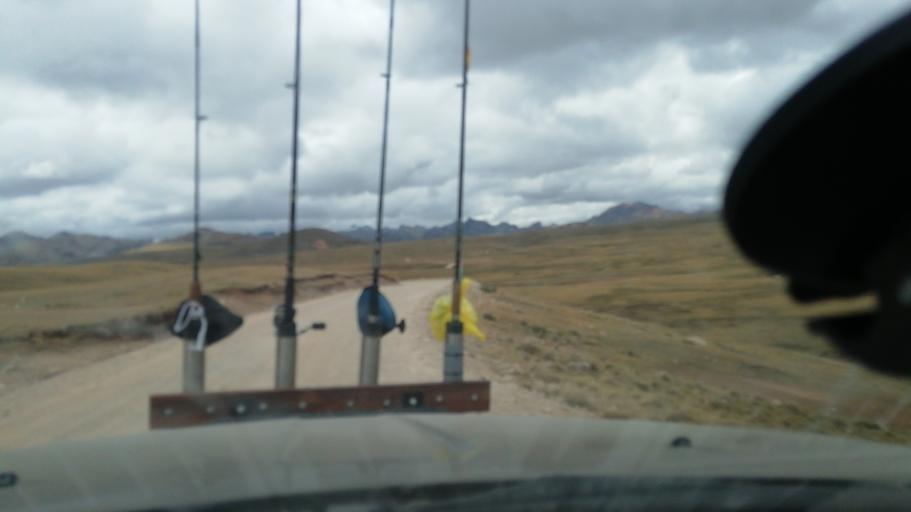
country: PE
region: Huancavelica
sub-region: Provincia de Huancavelica
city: Acobambilla
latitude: -12.5402
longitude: -75.5530
